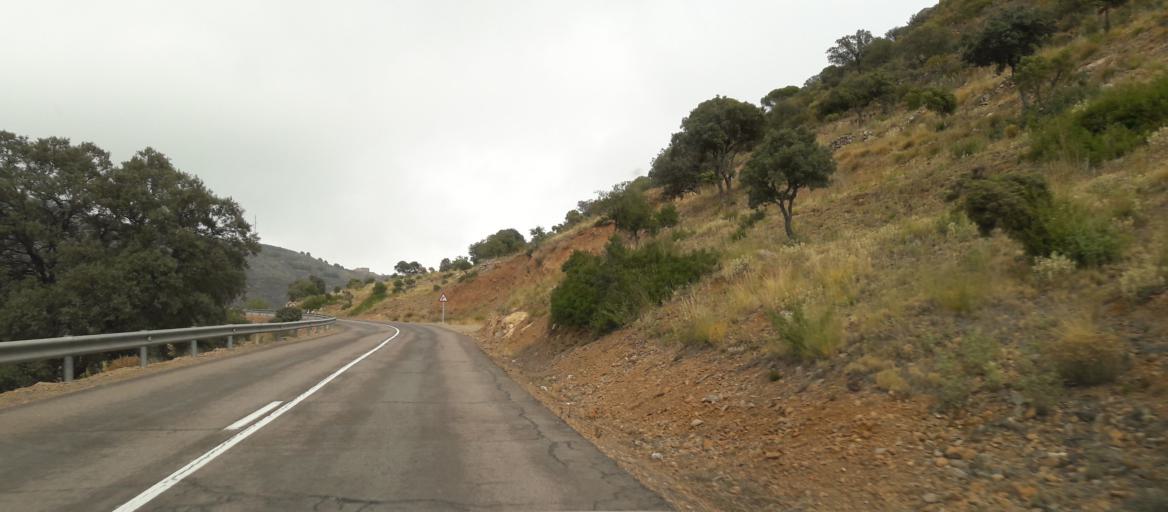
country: ES
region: Andalusia
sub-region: Provincia de Almeria
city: Enix
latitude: 36.8911
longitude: -2.6202
